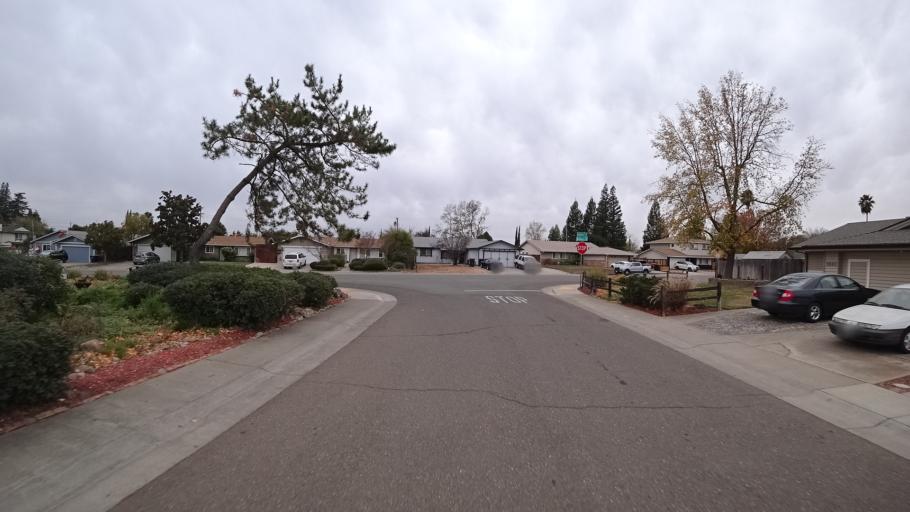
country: US
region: California
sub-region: Sacramento County
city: Citrus Heights
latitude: 38.6914
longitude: -121.3049
